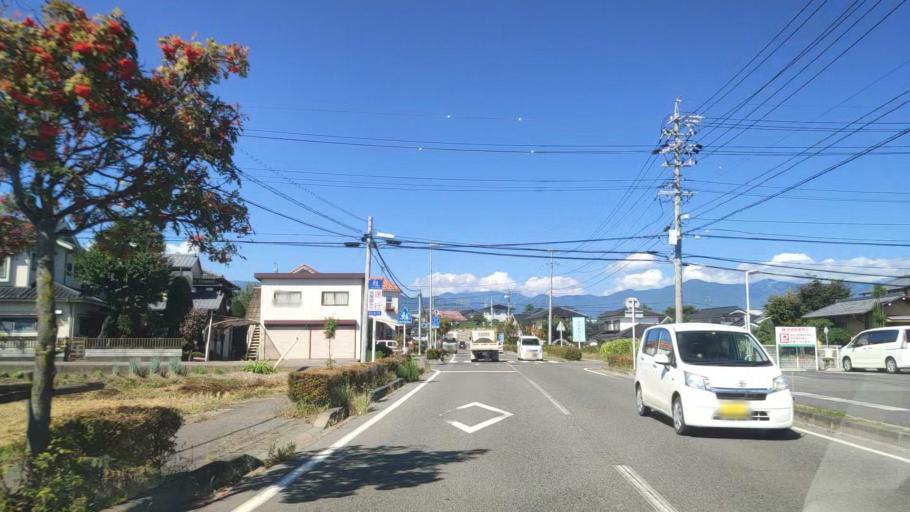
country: JP
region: Nagano
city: Shiojiri
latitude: 36.1651
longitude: 137.9354
